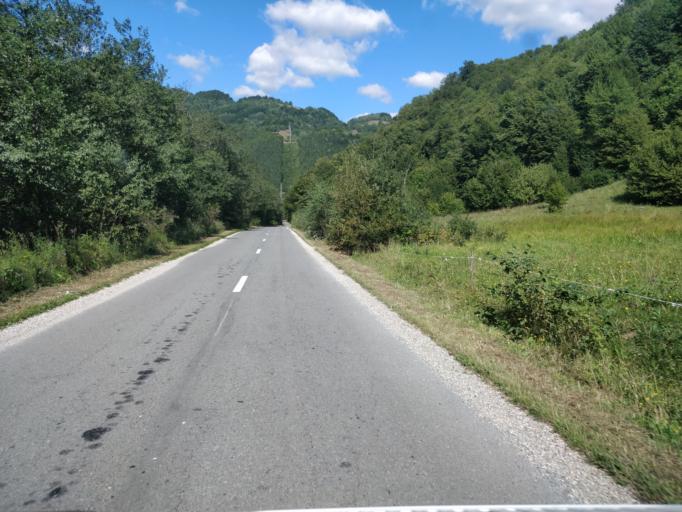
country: RO
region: Cluj
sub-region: Comuna Sacueu
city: Sacuieu
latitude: 46.8319
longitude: 22.8671
